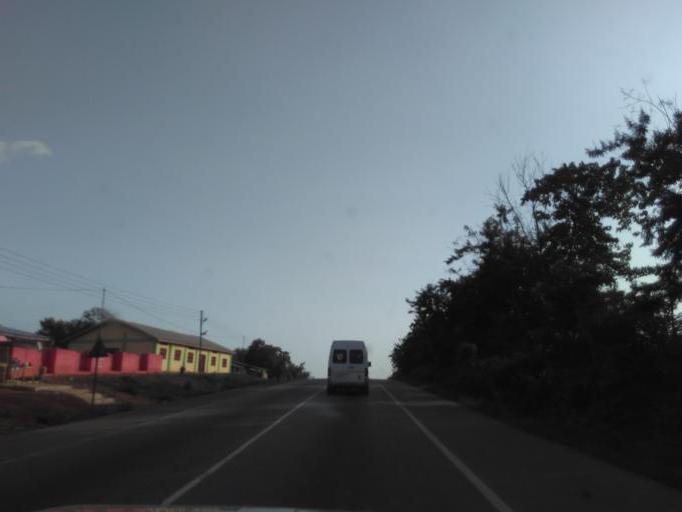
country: GH
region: Ashanti
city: Konongo
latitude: 6.6174
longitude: -1.2328
